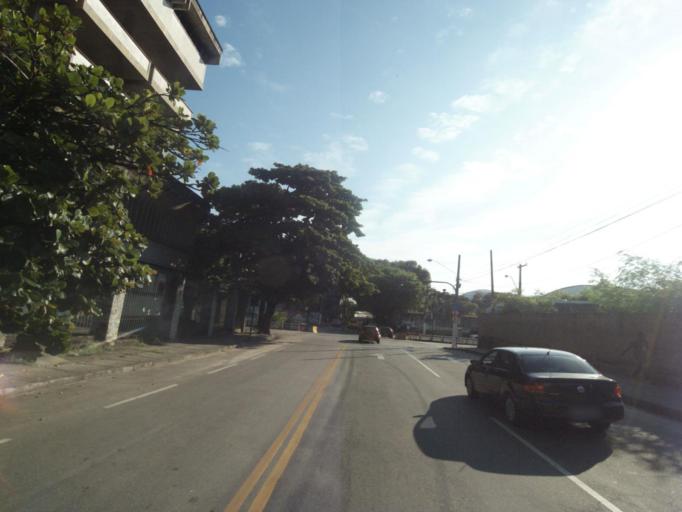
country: BR
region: Rio de Janeiro
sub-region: Niteroi
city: Niteroi
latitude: -22.8855
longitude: -43.1184
